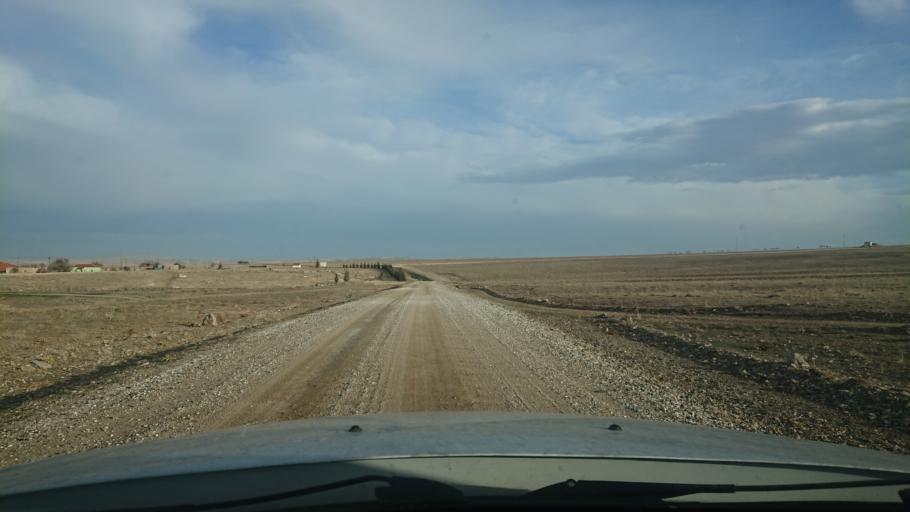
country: TR
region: Aksaray
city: Agacoren
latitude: 38.7128
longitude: 33.8687
